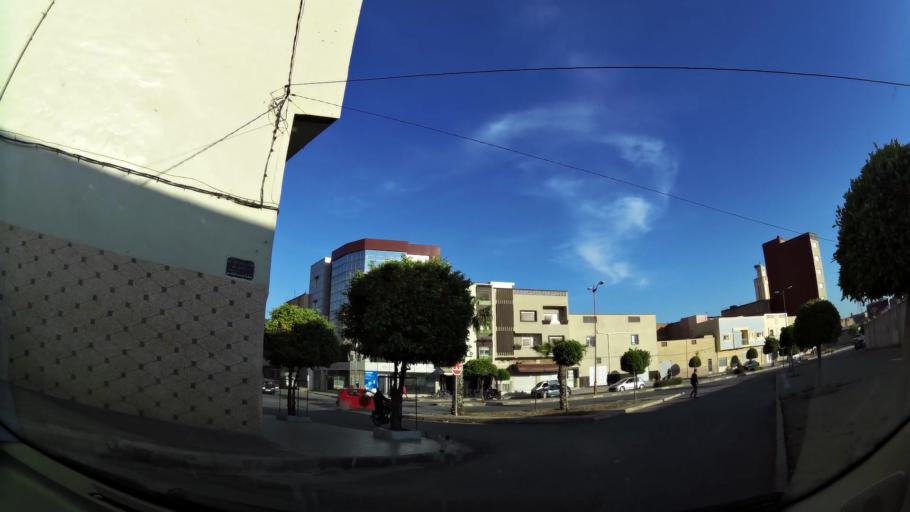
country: MA
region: Oriental
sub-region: Oujda-Angad
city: Oujda
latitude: 34.6948
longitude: -1.9052
